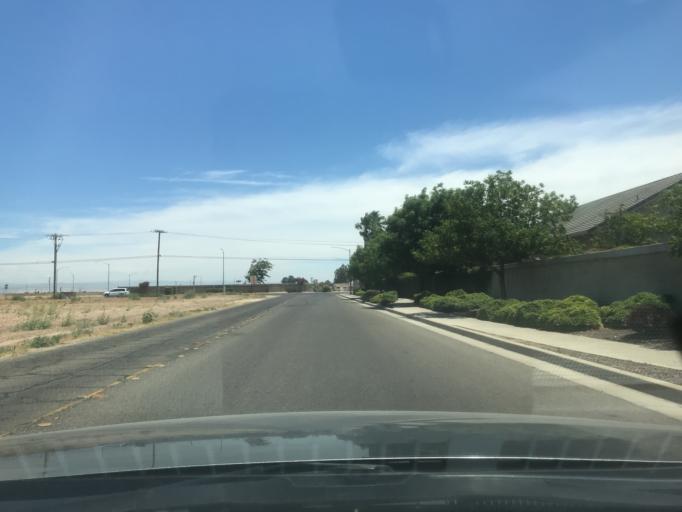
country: US
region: California
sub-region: Merced County
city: Winton
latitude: 37.3713
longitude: -120.5969
